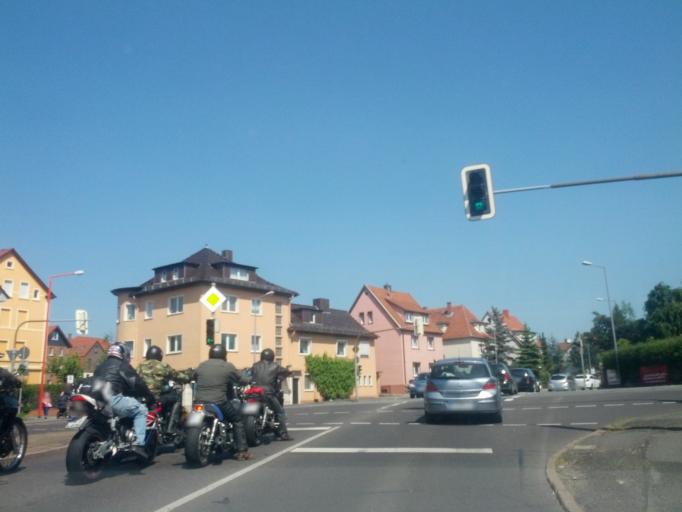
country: DE
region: Thuringia
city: Gotha
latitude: 50.9425
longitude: 10.7191
